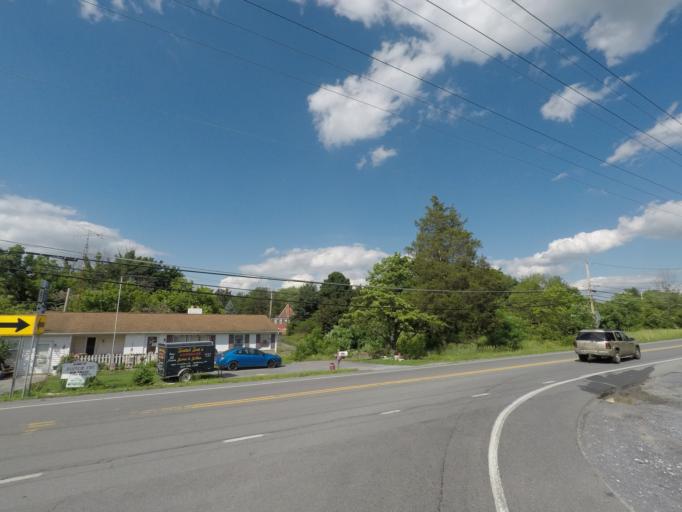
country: US
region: West Virginia
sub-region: Berkeley County
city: Martinsburg
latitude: 39.4225
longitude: -77.9251
